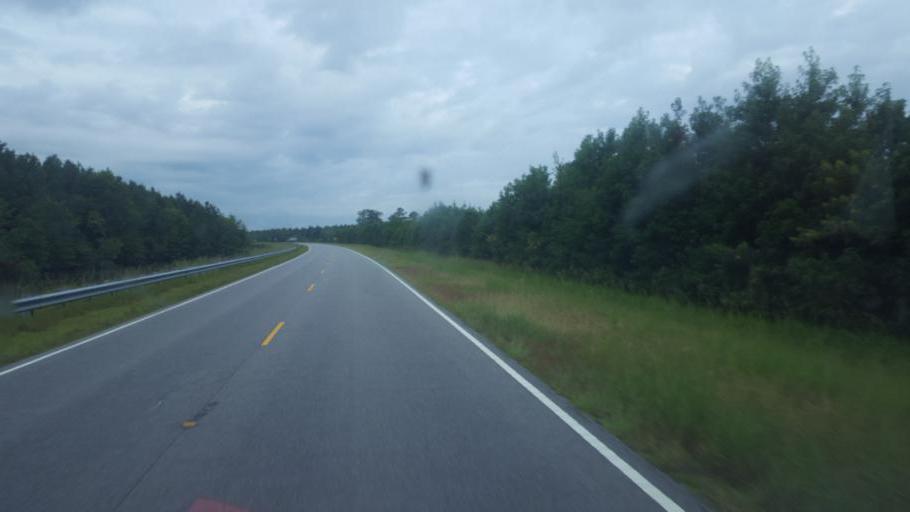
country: US
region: North Carolina
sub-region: Tyrrell County
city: Columbia
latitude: 35.9340
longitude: -76.1579
